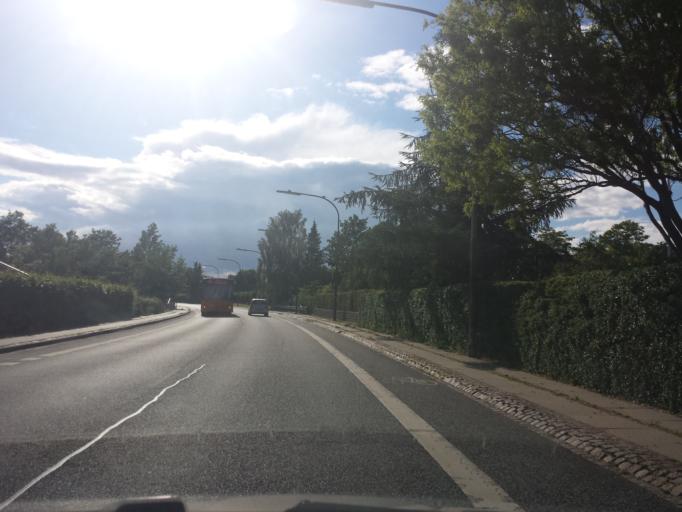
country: DK
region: Capital Region
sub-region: Ballerup Kommune
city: Malov
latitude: 55.7548
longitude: 12.3311
